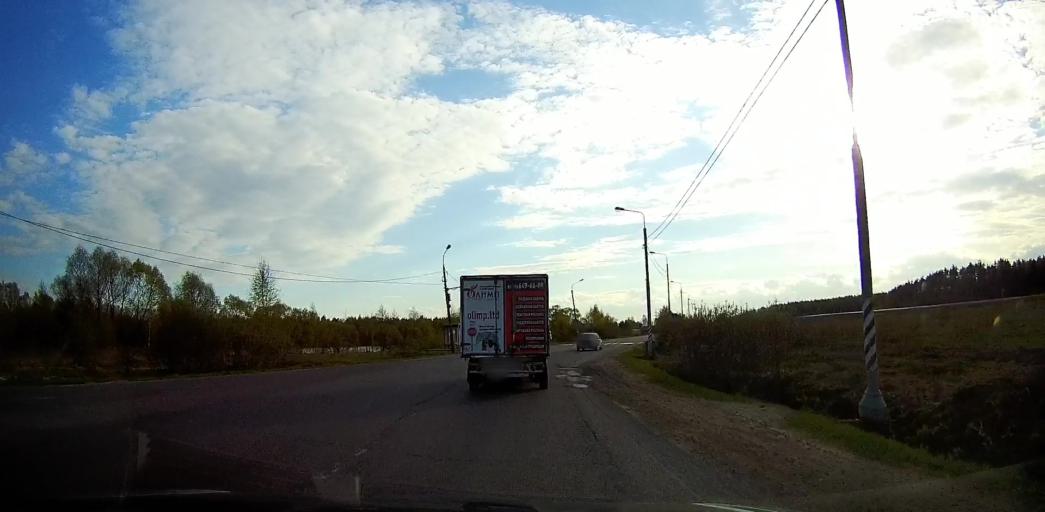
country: RU
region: Moskovskaya
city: Fryazevo
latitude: 55.7286
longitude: 38.4958
